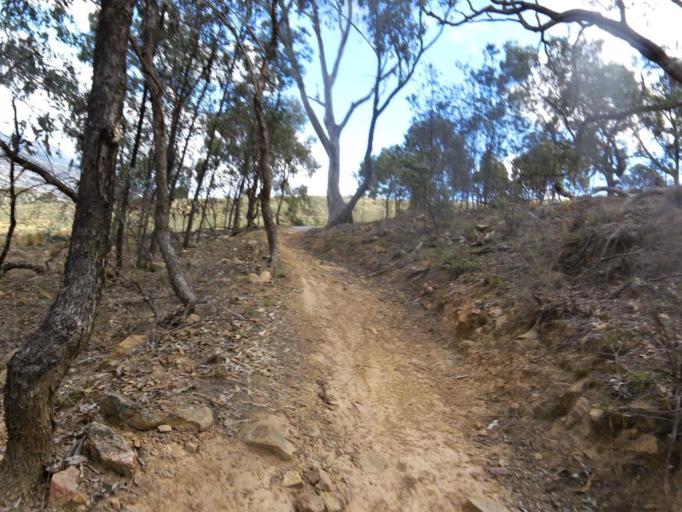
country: AU
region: Australian Capital Territory
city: Belconnen
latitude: -35.1408
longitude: 149.0934
